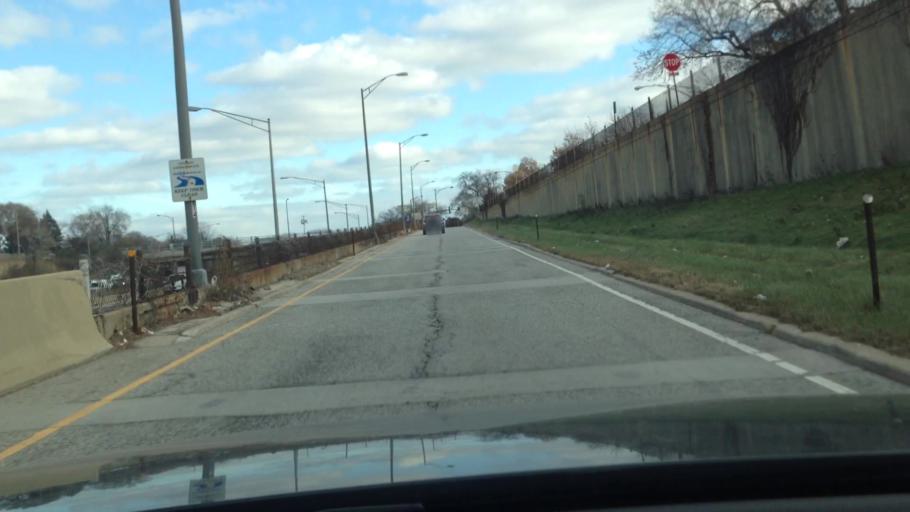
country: US
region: Illinois
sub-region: Cook County
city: Harwood Heights
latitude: 41.9822
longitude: -87.7908
